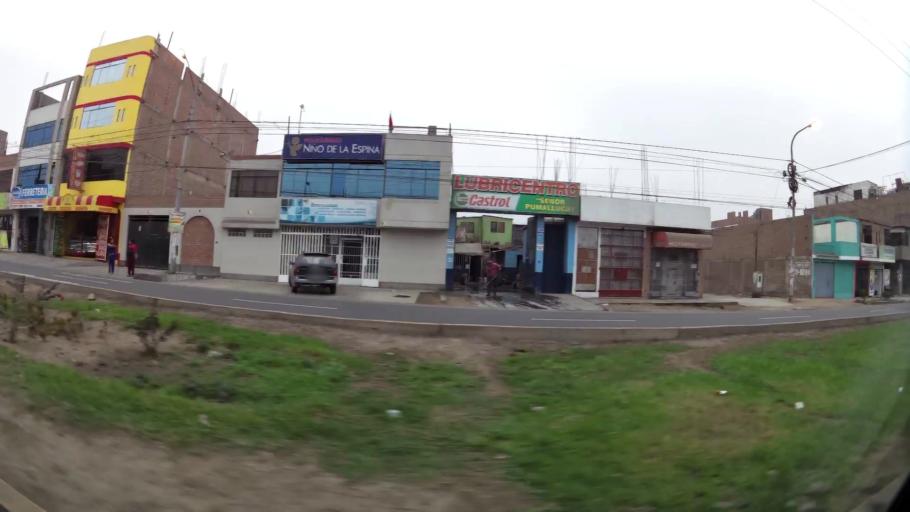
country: PE
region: Lima
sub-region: Lima
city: Urb. Santo Domingo
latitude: -11.8864
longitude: -77.0354
